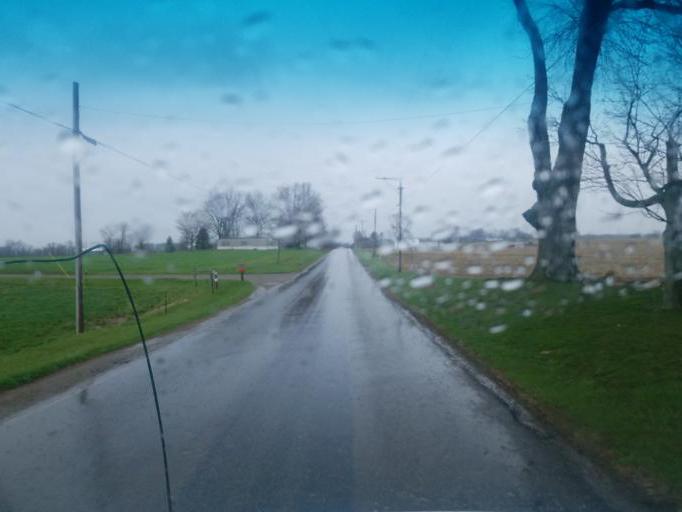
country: US
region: Ohio
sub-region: Wayne County
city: Apple Creek
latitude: 40.7208
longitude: -81.9154
